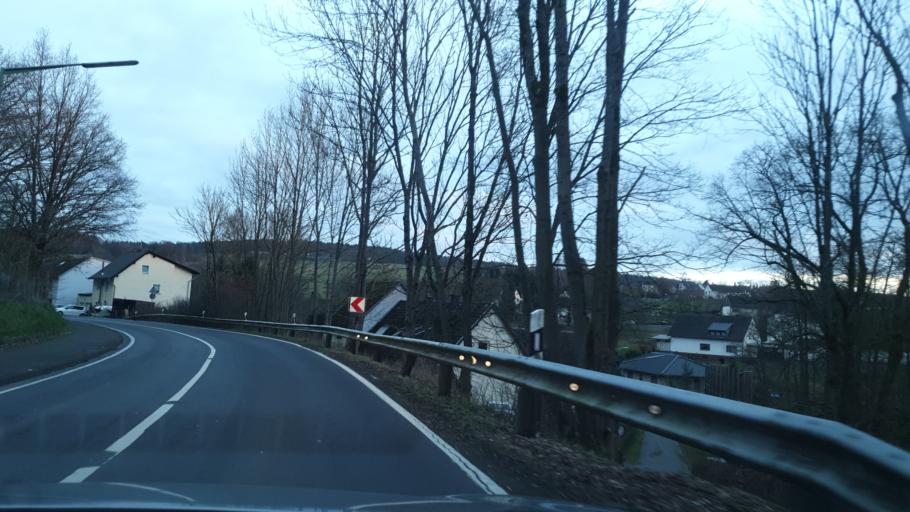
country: DE
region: Rheinland-Pfalz
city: Almersbach
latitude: 50.6746
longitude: 7.6287
